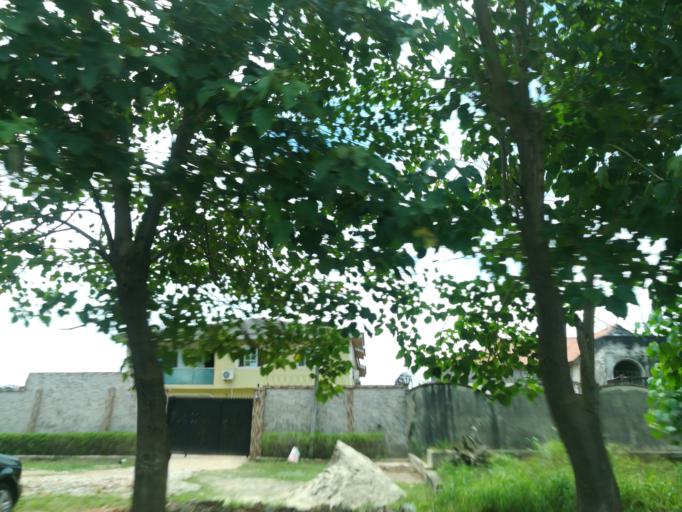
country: NG
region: Lagos
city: Ebute Ikorodu
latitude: 6.5912
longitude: 3.4925
